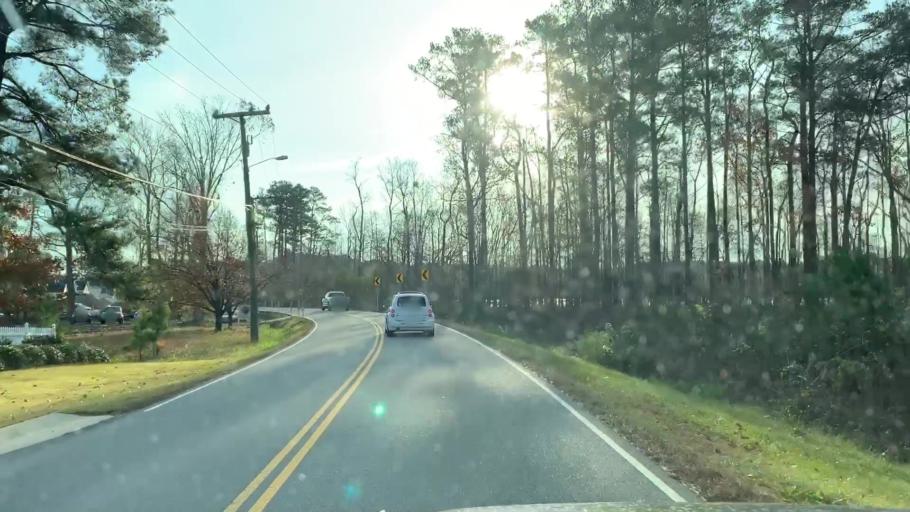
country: US
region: Virginia
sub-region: City of Chesapeake
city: Chesapeake
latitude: 36.7618
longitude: -76.1467
